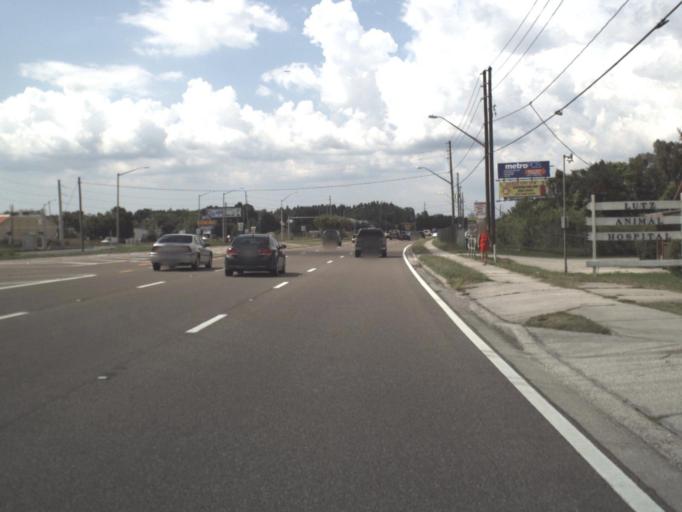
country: US
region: Florida
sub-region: Hillsborough County
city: Lutz
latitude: 28.1827
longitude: -82.4659
